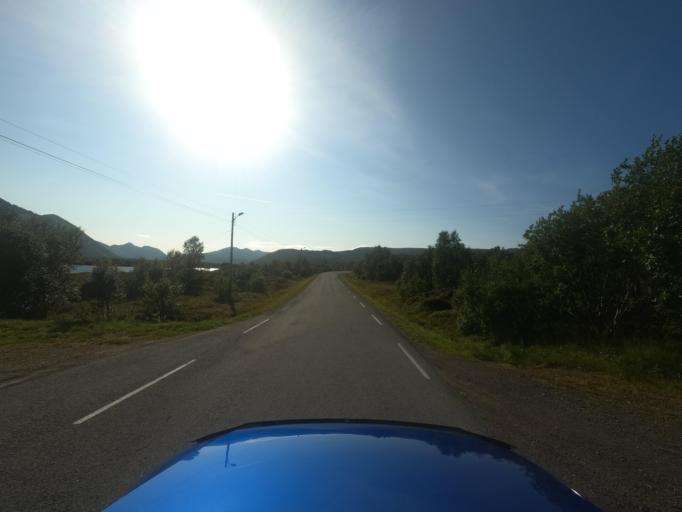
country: NO
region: Nordland
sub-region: Vestvagoy
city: Evjen
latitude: 68.3037
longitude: 13.8744
